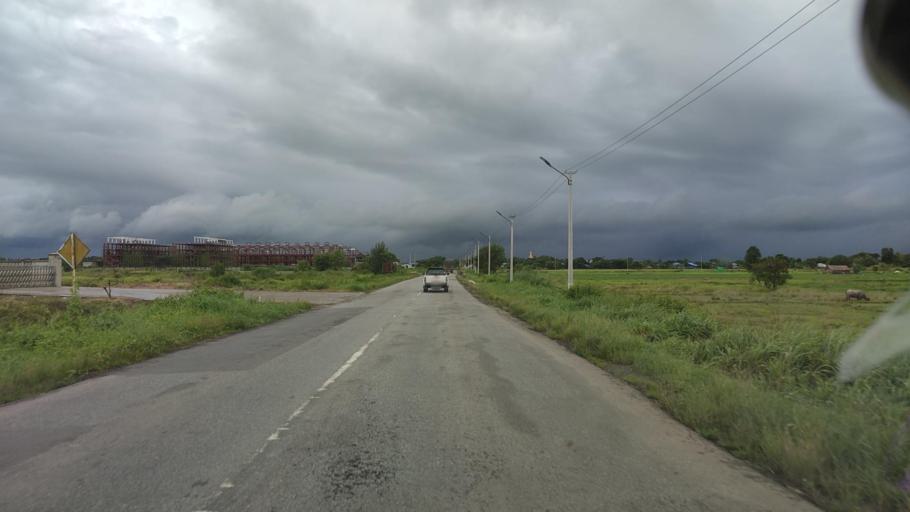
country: MM
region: Bago
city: Bago
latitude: 17.3880
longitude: 96.5070
